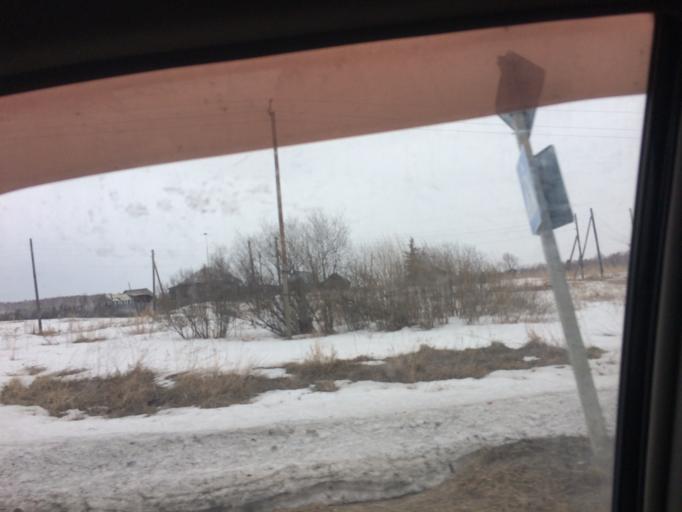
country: RU
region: Novosibirsk
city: Tashara
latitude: 55.4203
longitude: 83.4829
